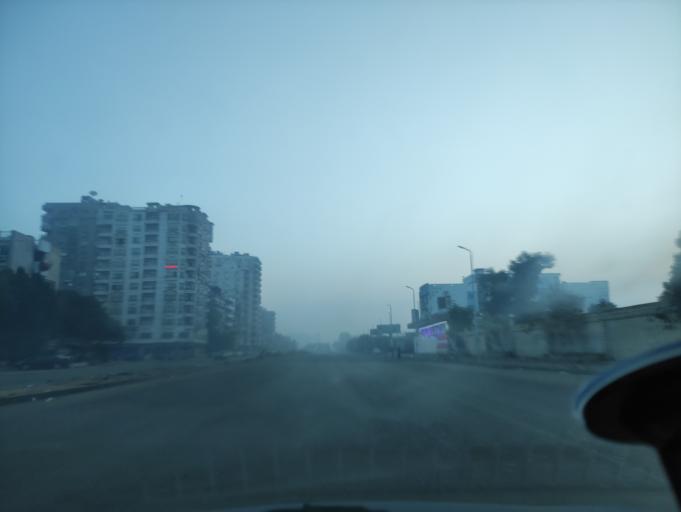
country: EG
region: Muhafazat al Qahirah
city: Cairo
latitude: 30.0459
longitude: 31.3504
